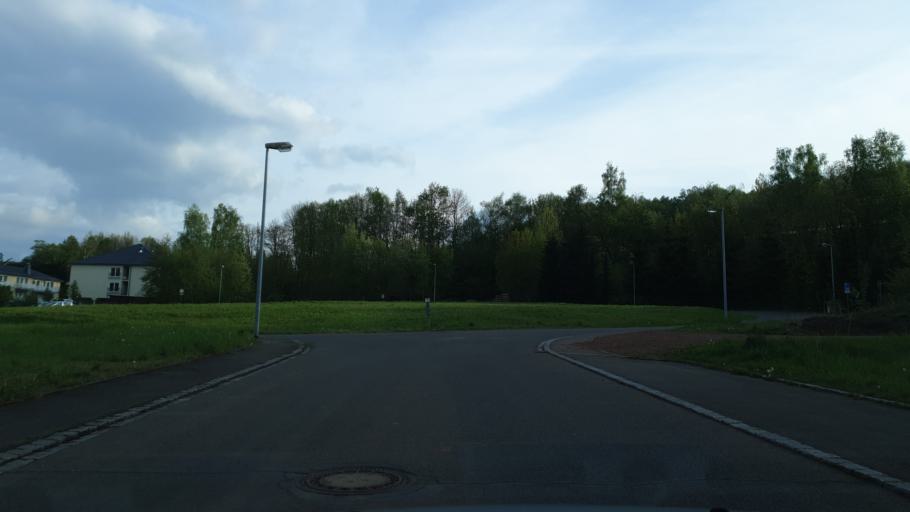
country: DE
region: Saxony
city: Oelsnitz
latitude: 50.7283
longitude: 12.6946
